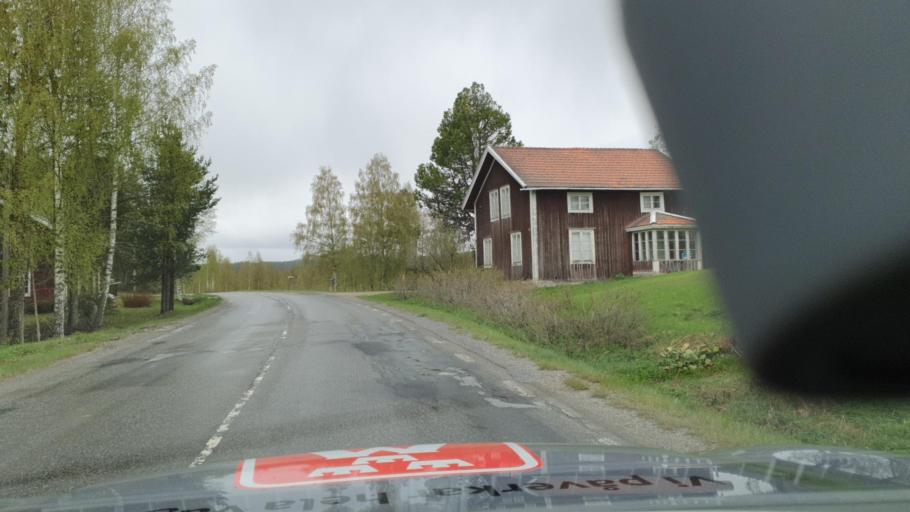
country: SE
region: Vaesternorrland
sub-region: OErnskoeldsviks Kommun
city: Bredbyn
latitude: 63.4682
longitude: 17.9827
